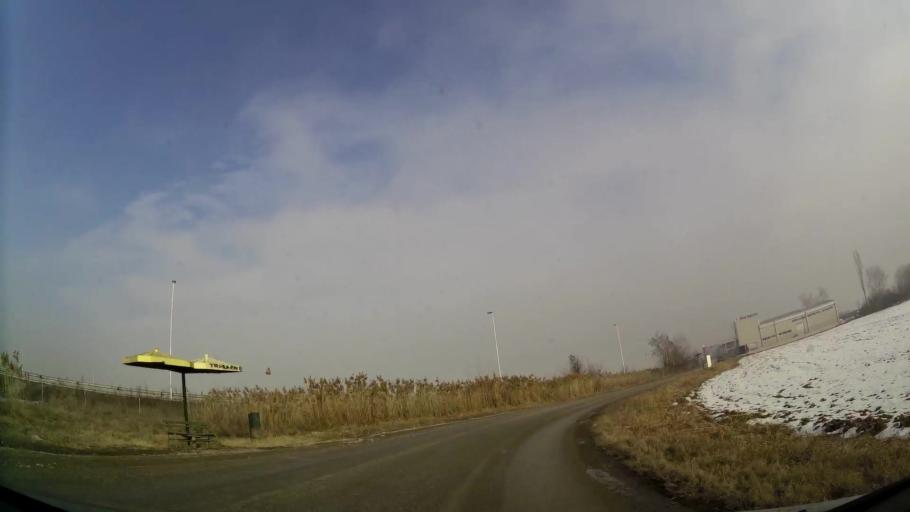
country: MK
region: Ilinden
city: Jurumleri
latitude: 41.9924
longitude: 21.5356
